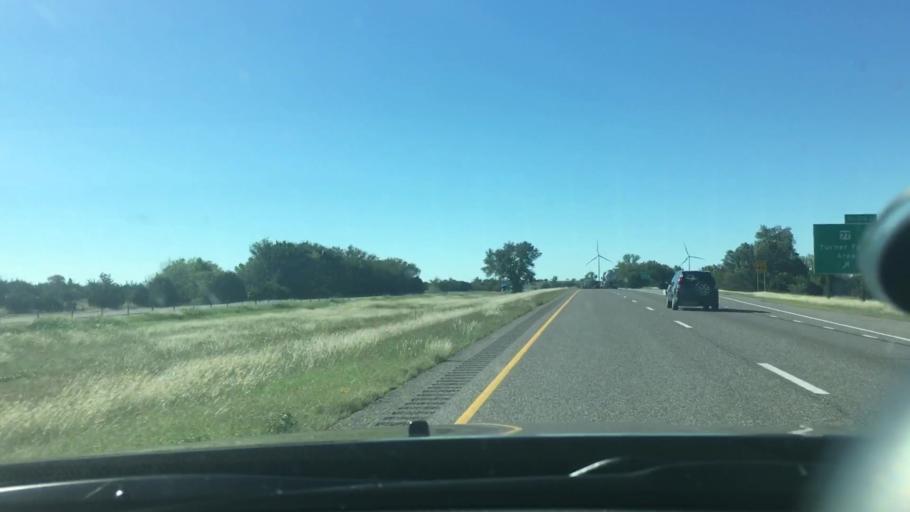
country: US
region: Oklahoma
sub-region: Murray County
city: Davis
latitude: 34.4051
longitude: -97.1404
